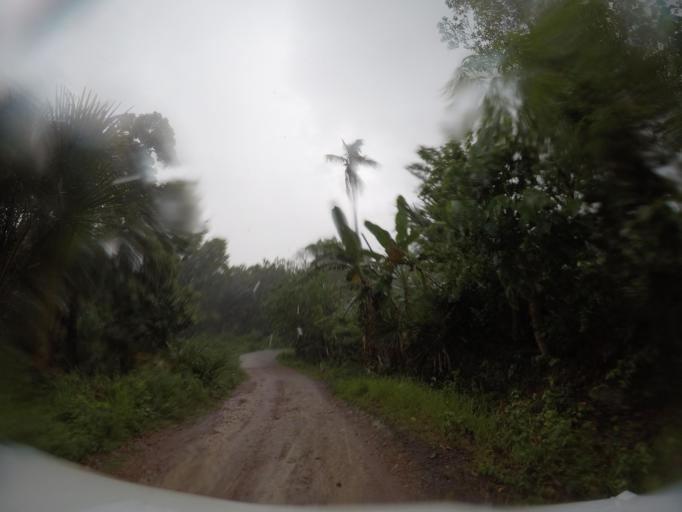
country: TL
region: Baucau
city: Venilale
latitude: -8.6295
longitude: 126.4407
